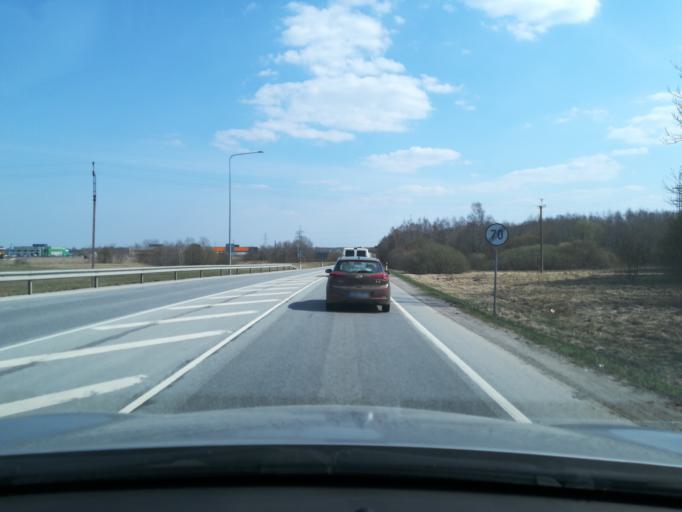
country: EE
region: Harju
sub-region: Harku vald
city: Tabasalu
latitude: 59.3904
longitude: 24.5610
